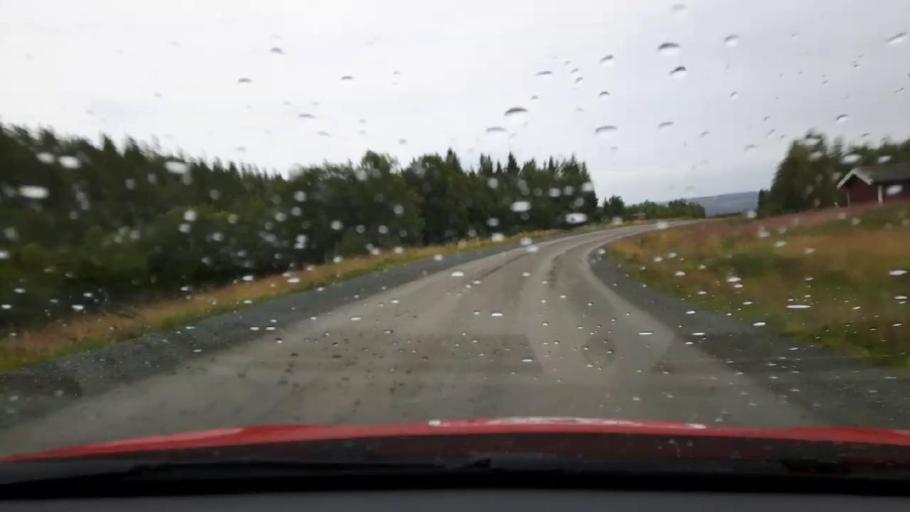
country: SE
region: Jaemtland
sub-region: Are Kommun
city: Are
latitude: 63.4751
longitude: 12.5597
